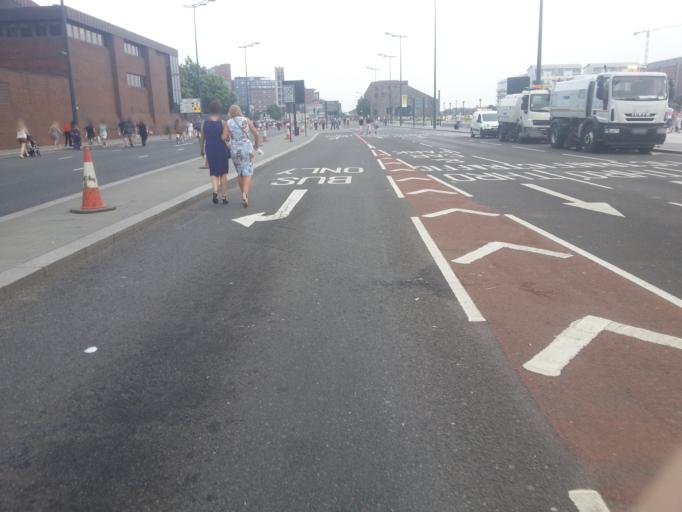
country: GB
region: England
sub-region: Liverpool
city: Liverpool
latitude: 53.4016
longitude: -2.9891
